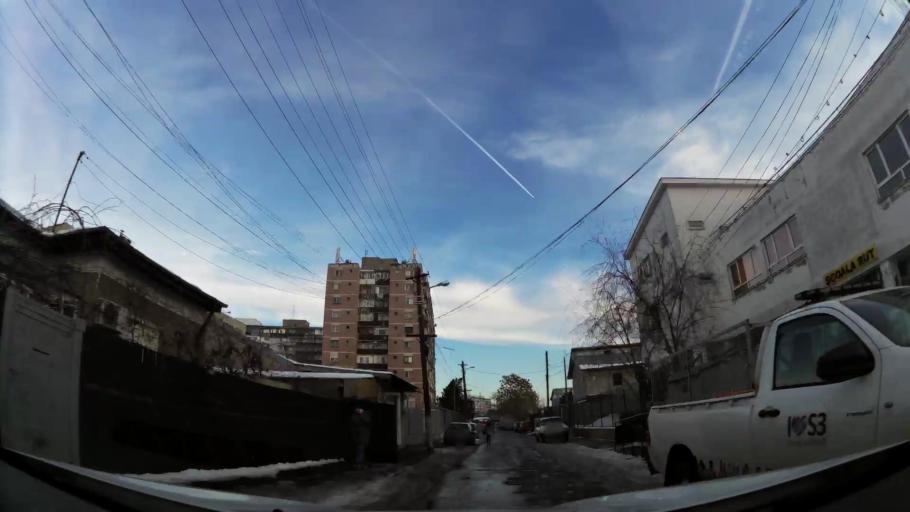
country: RO
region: Bucuresti
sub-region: Municipiul Bucuresti
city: Bucuresti
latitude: 44.3933
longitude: 26.0805
